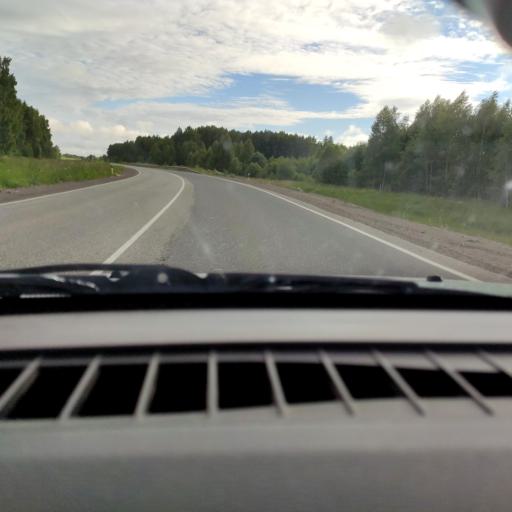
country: RU
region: Perm
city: Kungur
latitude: 57.3342
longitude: 56.9661
